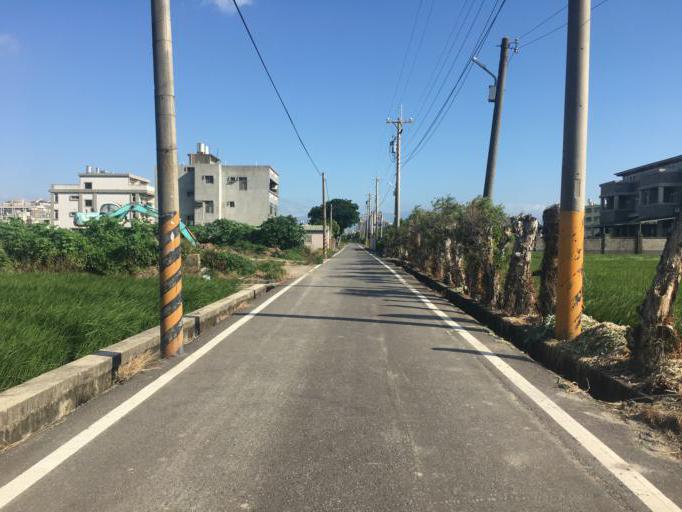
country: TW
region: Taiwan
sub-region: Hsinchu
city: Zhubei
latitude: 24.8395
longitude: 120.9888
